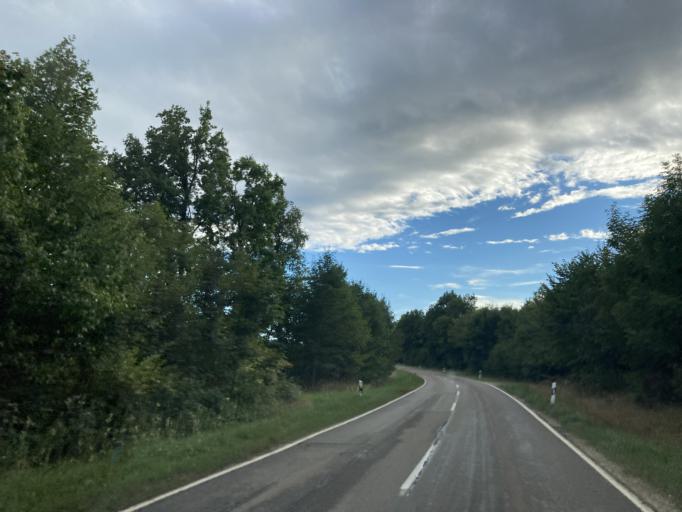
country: DE
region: Bavaria
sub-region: Swabia
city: Amerdingen
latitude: 48.7303
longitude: 10.4545
